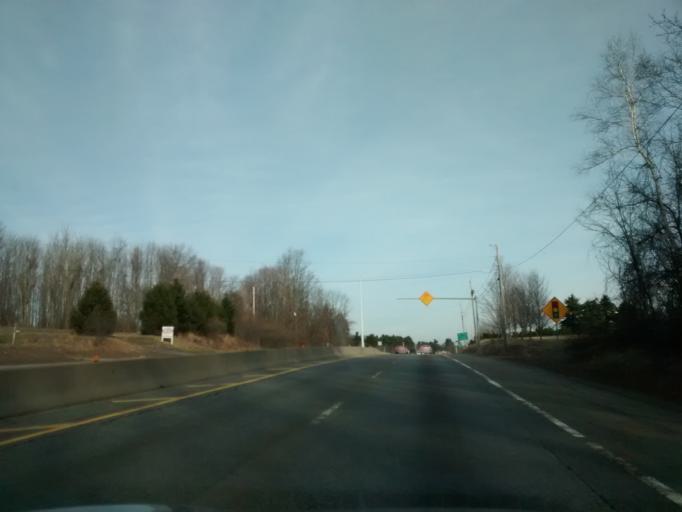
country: US
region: Massachusetts
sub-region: Worcester County
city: Charlton
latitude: 42.1463
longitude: -71.9728
